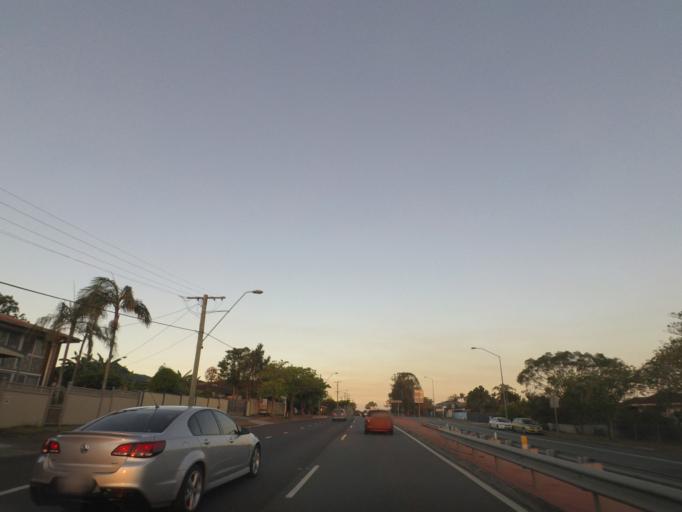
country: AU
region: Queensland
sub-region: Brisbane
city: Upper Mount Gravatt
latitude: -27.5551
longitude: 153.0973
